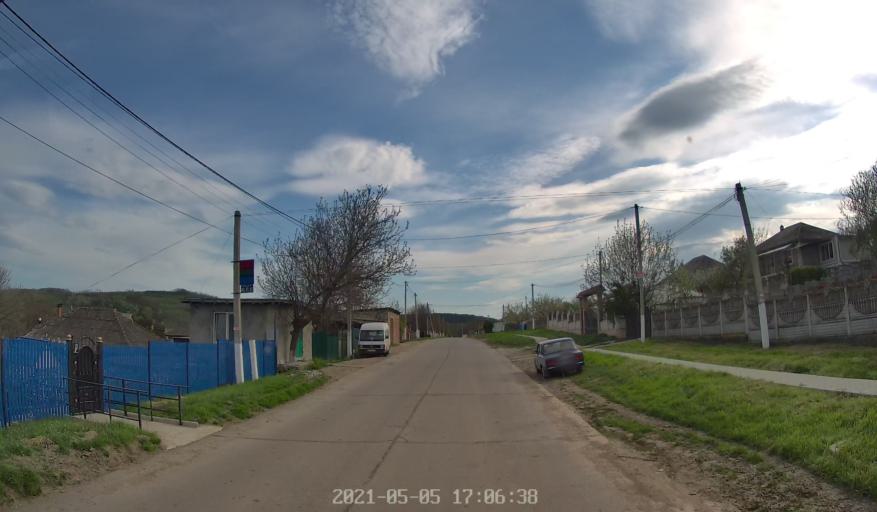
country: MD
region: Chisinau
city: Vadul lui Voda
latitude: 47.0187
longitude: 29.1387
